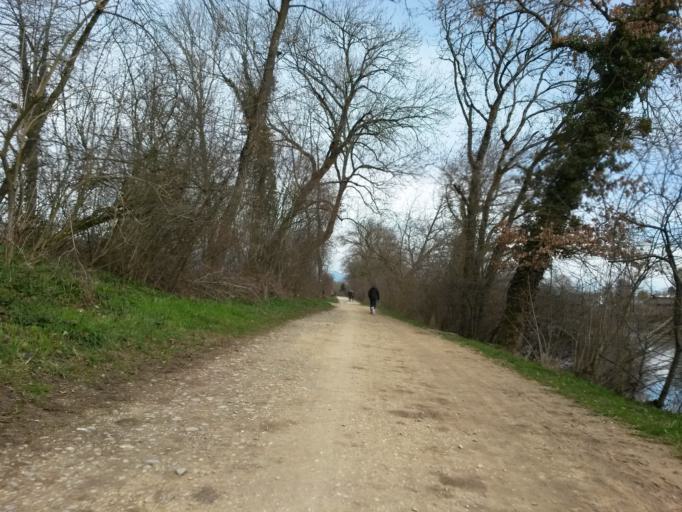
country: CH
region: Bern
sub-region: Biel/Bienne District
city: Orpund
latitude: 47.1289
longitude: 7.2992
